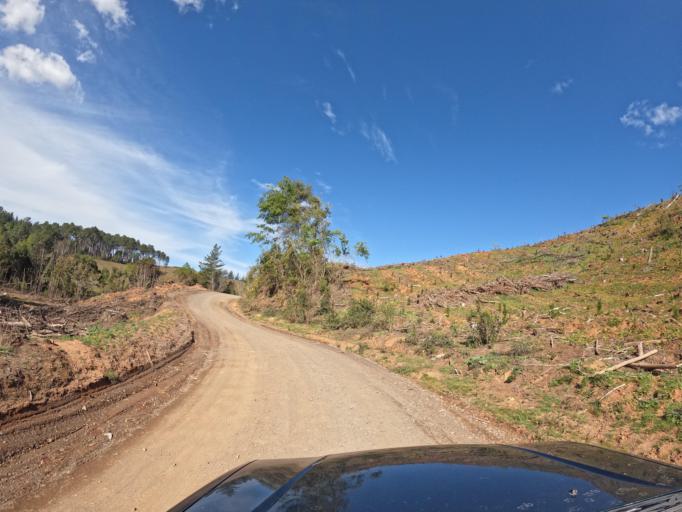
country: CL
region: Biobio
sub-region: Provincia de Biobio
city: La Laja
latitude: -37.0803
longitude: -72.8367
